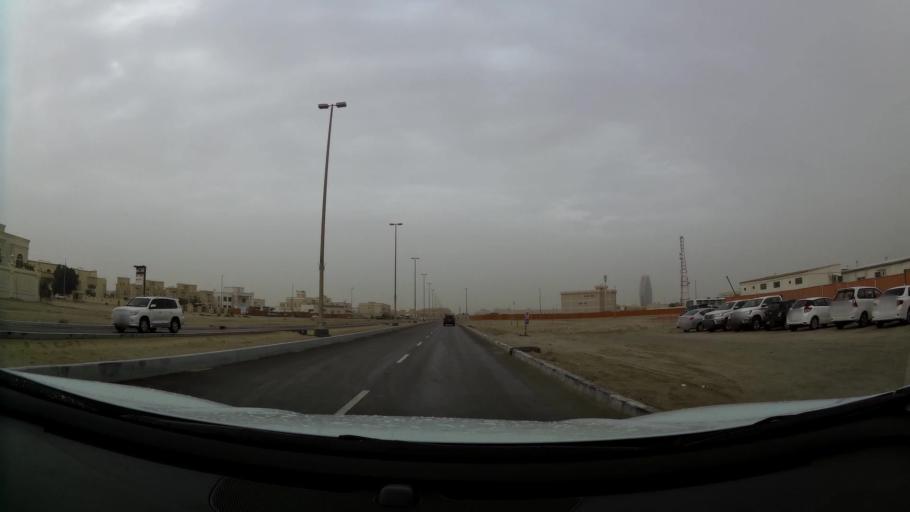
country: AE
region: Abu Dhabi
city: Abu Dhabi
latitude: 24.4301
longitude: 54.5818
